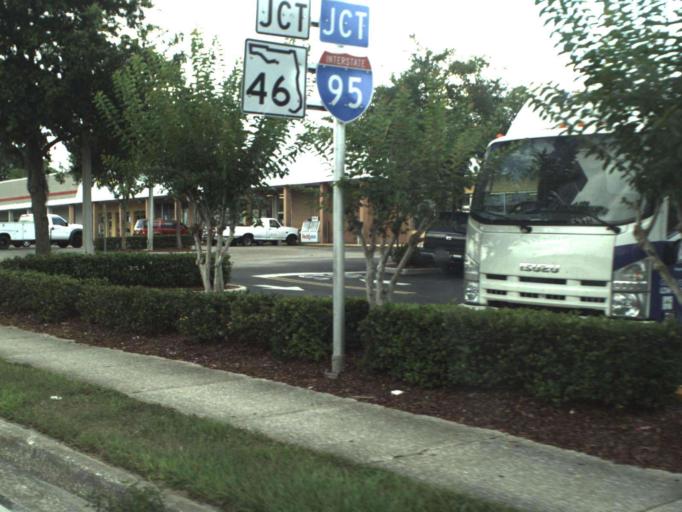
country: US
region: Florida
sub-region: Seminole County
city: Sanford
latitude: 28.7881
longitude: -81.2731
